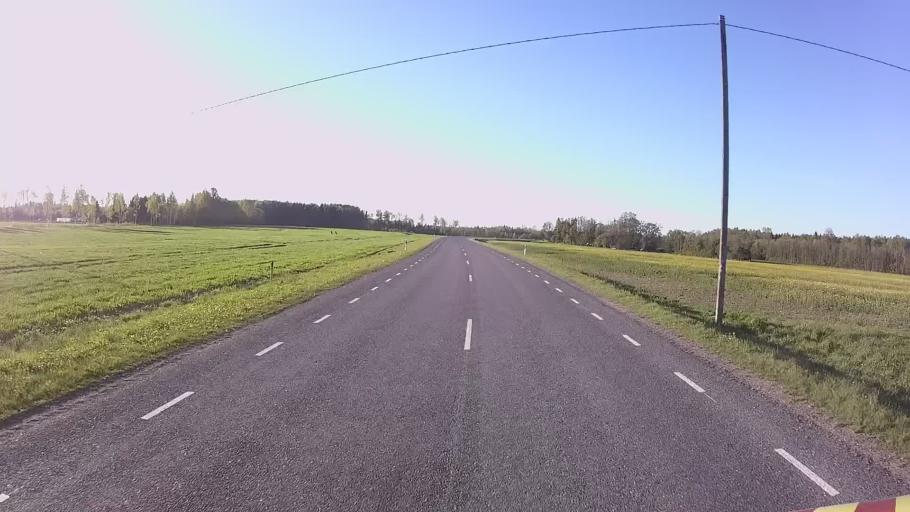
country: EE
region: Jogevamaa
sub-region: Poltsamaa linn
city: Poltsamaa
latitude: 58.4960
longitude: 25.8338
